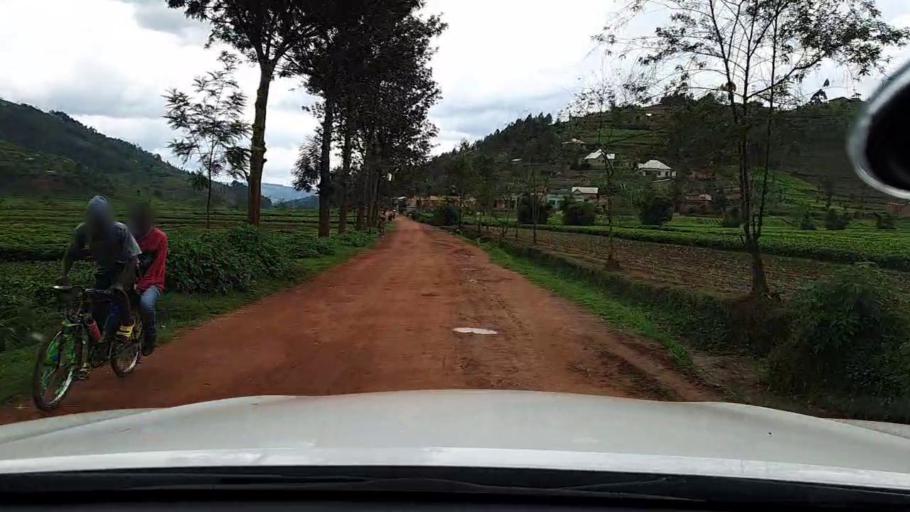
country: RW
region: Northern Province
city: Byumba
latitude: -1.6693
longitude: 29.9249
